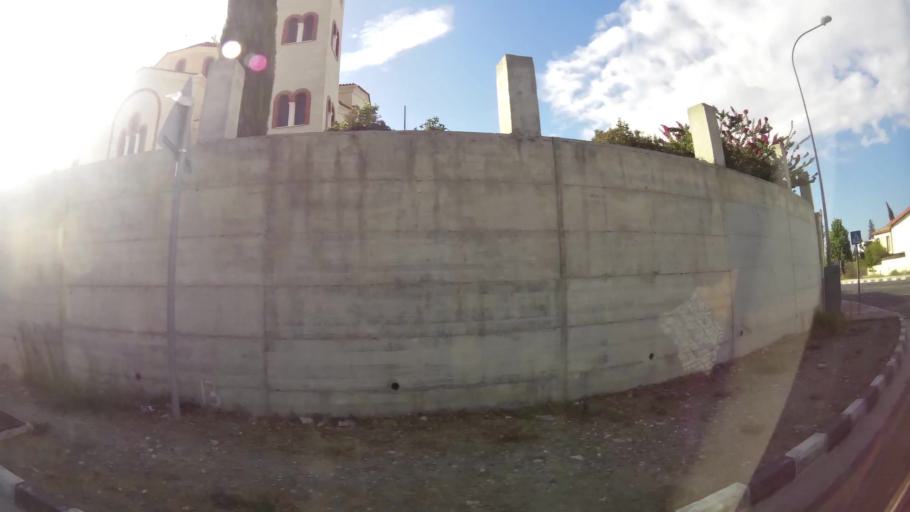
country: CY
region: Lefkosia
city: Nicosia
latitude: 35.1348
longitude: 33.3661
